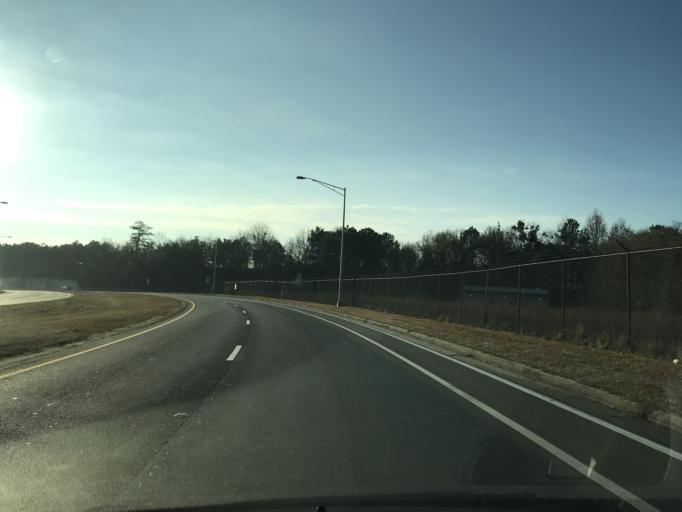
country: US
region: Georgia
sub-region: Fulton County
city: College Park
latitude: 33.6193
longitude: -84.4524
